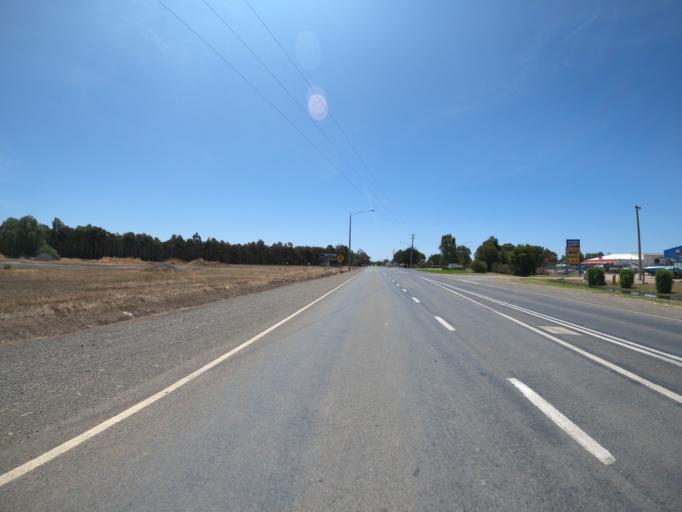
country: AU
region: Victoria
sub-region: Moira
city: Yarrawonga
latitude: -36.0277
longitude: 145.9955
